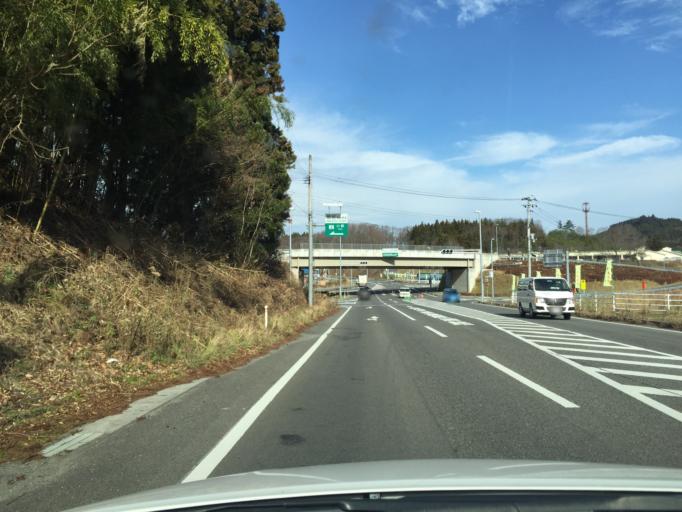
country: JP
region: Fukushima
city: Funehikimachi-funehiki
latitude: 37.2901
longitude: 140.6172
